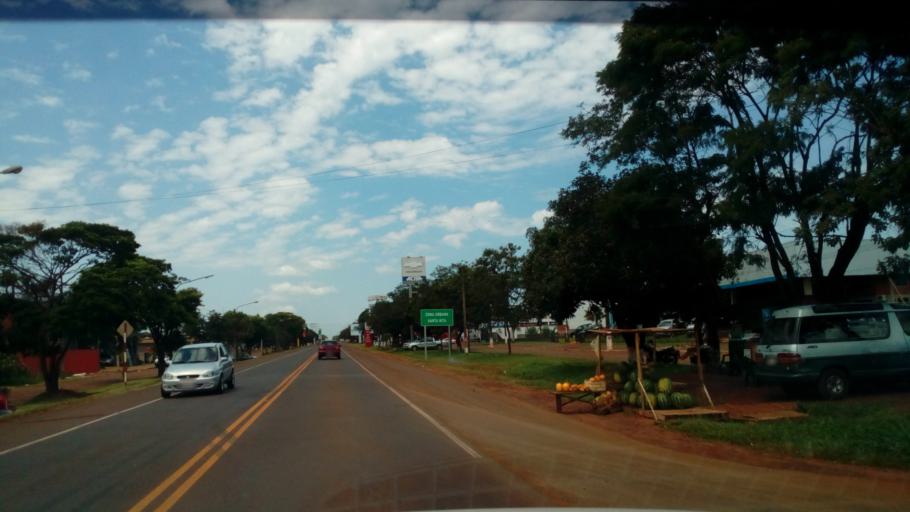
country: PY
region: Alto Parana
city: Santa Rita
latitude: -25.7744
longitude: -55.0732
